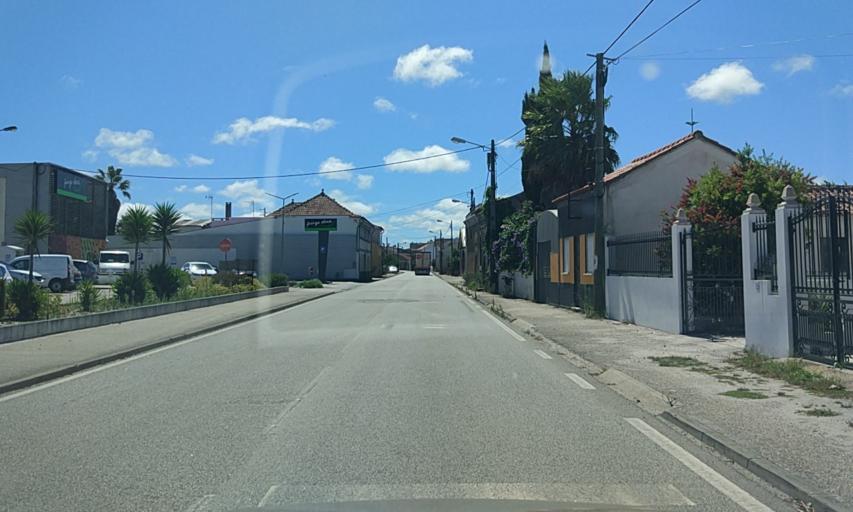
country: PT
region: Coimbra
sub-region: Mira
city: Mira
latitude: 40.4363
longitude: -8.7284
